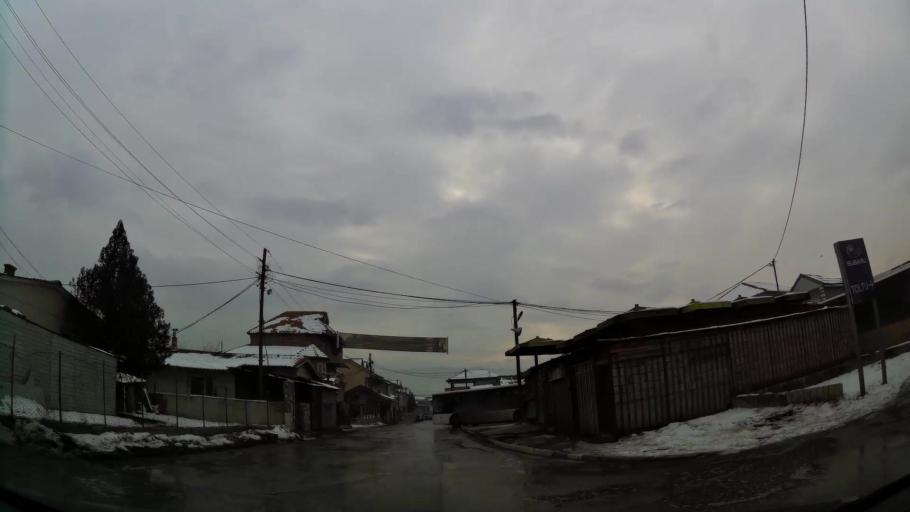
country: MK
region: Suto Orizari
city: Suto Orizare
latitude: 42.0451
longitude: 21.4272
